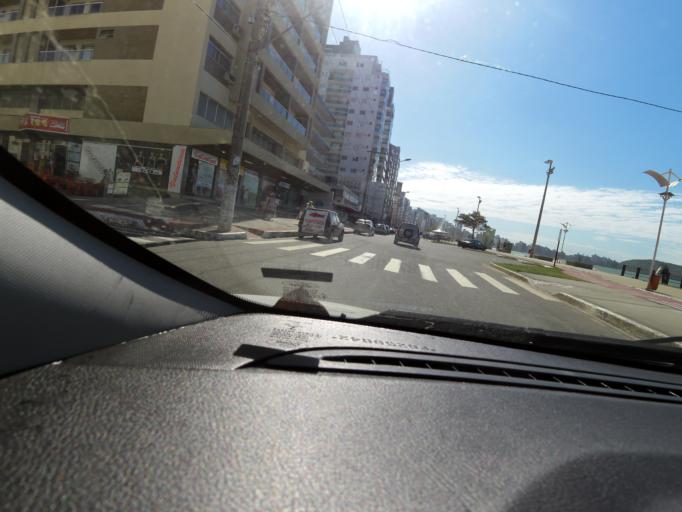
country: BR
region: Espirito Santo
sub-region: Guarapari
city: Guarapari
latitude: -20.6573
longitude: -40.4924
